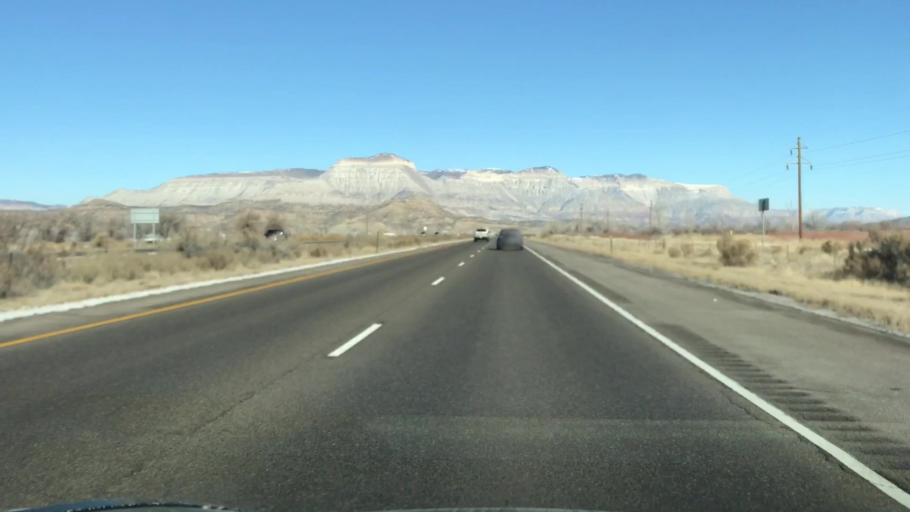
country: US
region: Colorado
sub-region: Garfield County
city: Parachute
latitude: 39.3092
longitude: -108.2153
